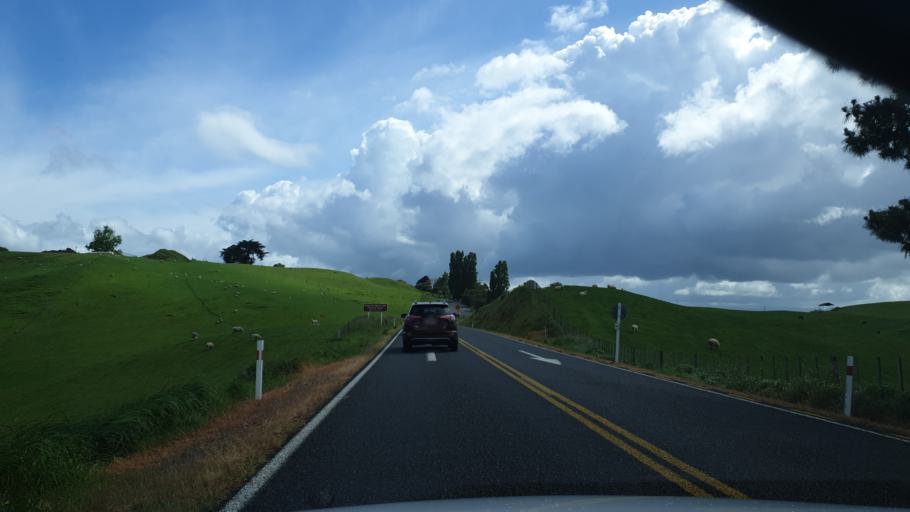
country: NZ
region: Waikato
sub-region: Matamata-Piako District
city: Matamata
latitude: -37.8752
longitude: 175.6854
